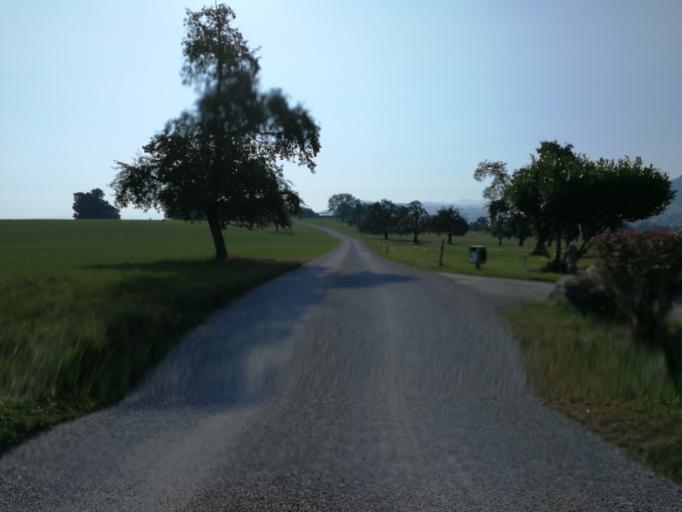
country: CH
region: Zurich
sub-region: Bezirk Horgen
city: Waedenswil / Eichweid
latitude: 47.1998
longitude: 8.6616
